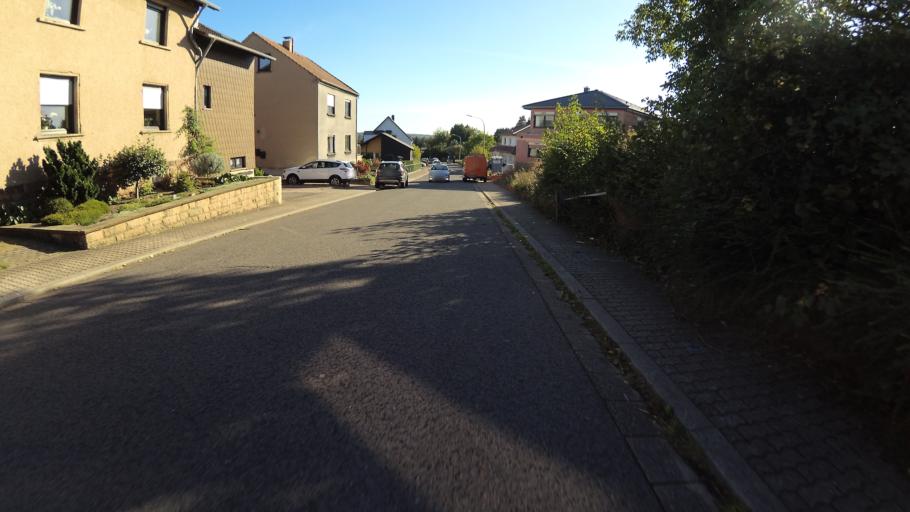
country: DE
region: Saarland
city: Eppelborn
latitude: 49.3579
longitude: 6.9790
